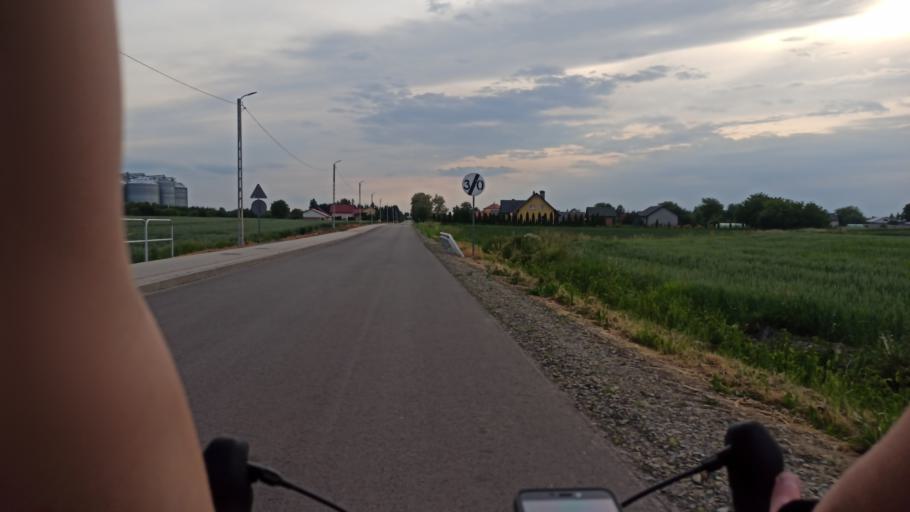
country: PL
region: Subcarpathian Voivodeship
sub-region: Powiat jaroslawski
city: Sosnica
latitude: 49.8973
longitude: 22.8356
